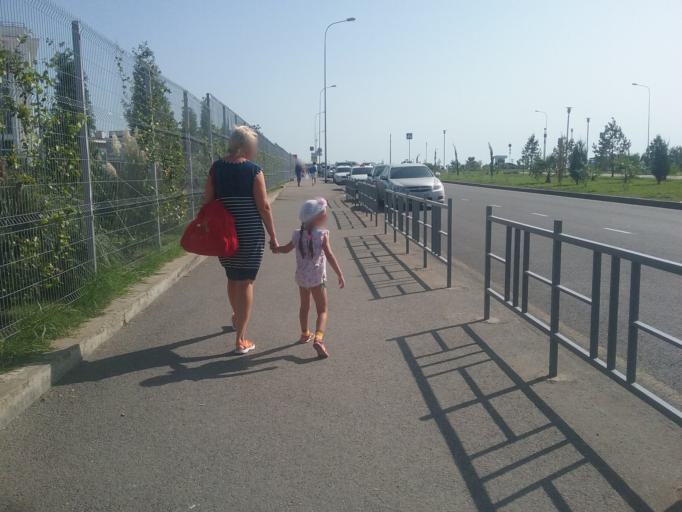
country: RU
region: Krasnodarskiy
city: Adler
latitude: 43.3877
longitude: 39.9913
